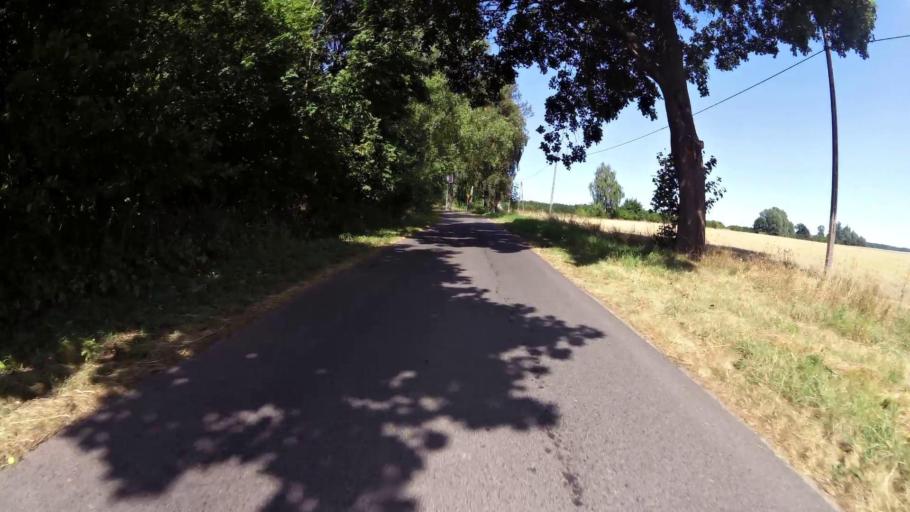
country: PL
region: West Pomeranian Voivodeship
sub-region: Powiat stargardzki
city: Suchan
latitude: 53.2952
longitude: 15.3649
